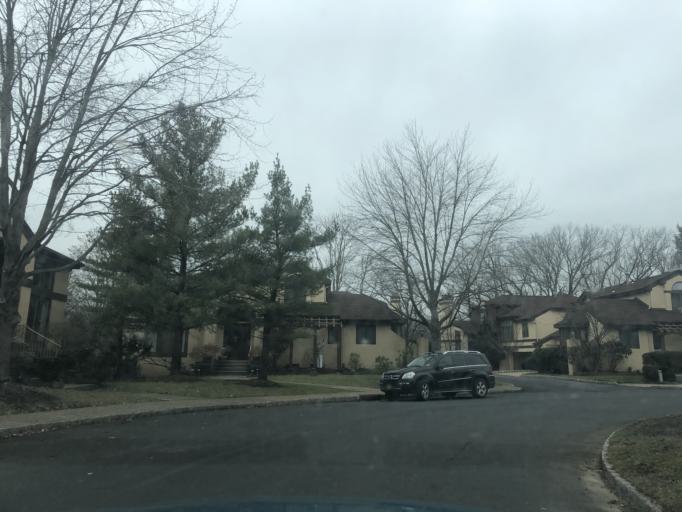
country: US
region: New Jersey
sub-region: Somerset County
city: Kingston
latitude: 40.3518
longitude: -74.6244
